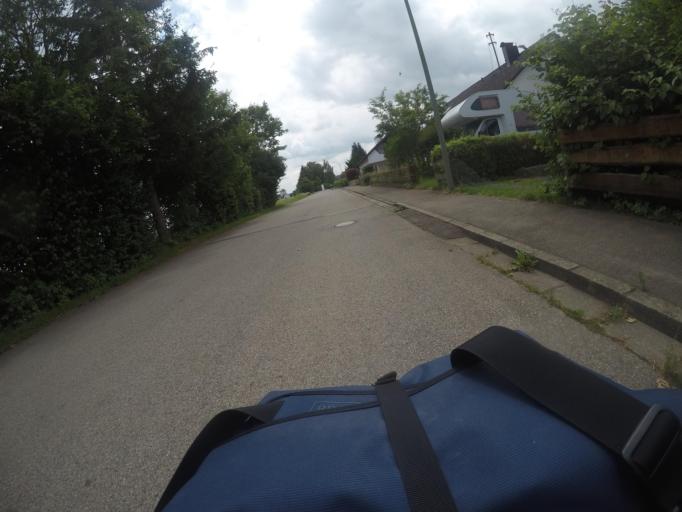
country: DE
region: Bavaria
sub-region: Swabia
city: Heimertingen
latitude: 48.0413
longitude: 10.1592
